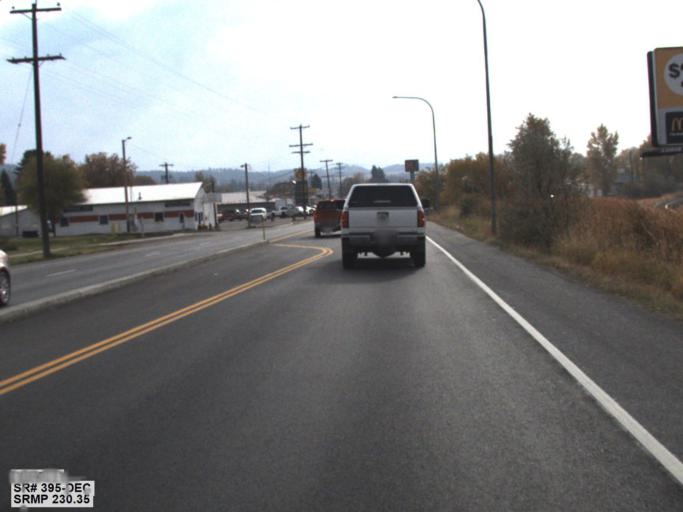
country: US
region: Washington
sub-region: Stevens County
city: Colville
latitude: 48.5524
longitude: -117.9167
